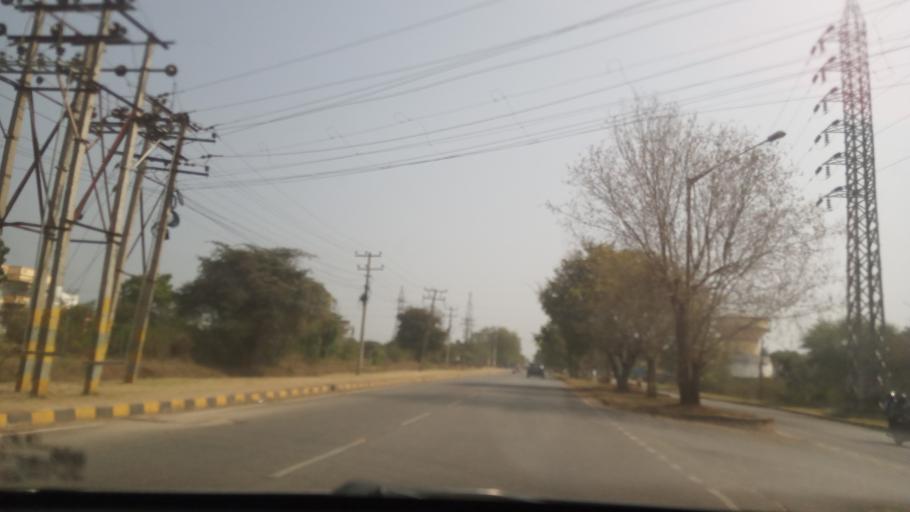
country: IN
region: Karnataka
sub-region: Mysore
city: Mysore
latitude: 12.2885
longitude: 76.6193
